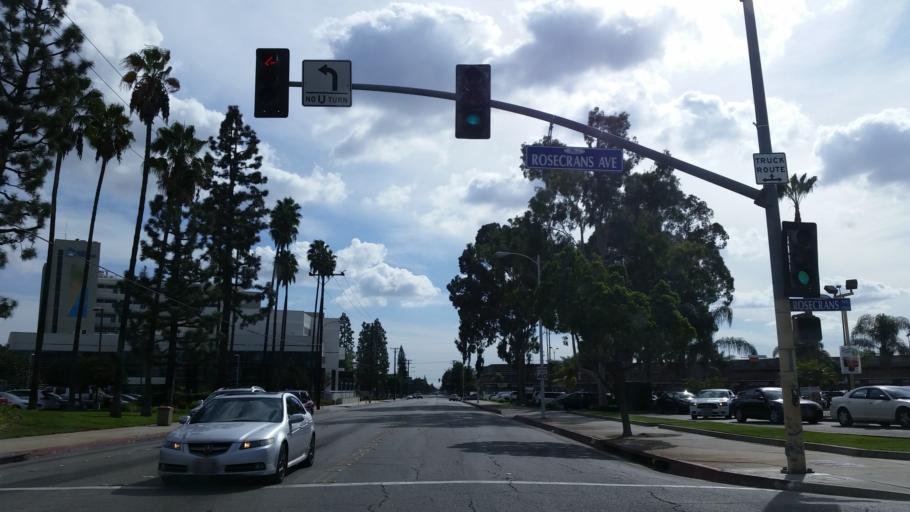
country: US
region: California
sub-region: Los Angeles County
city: Bellflower
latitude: 33.9041
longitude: -118.1341
